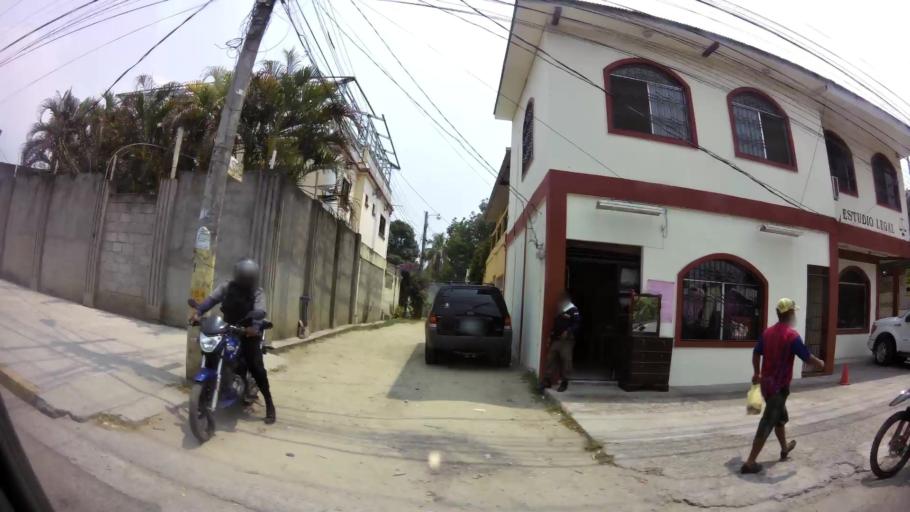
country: HN
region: Cortes
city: San Pedro Sula
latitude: 15.4866
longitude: -88.0181
